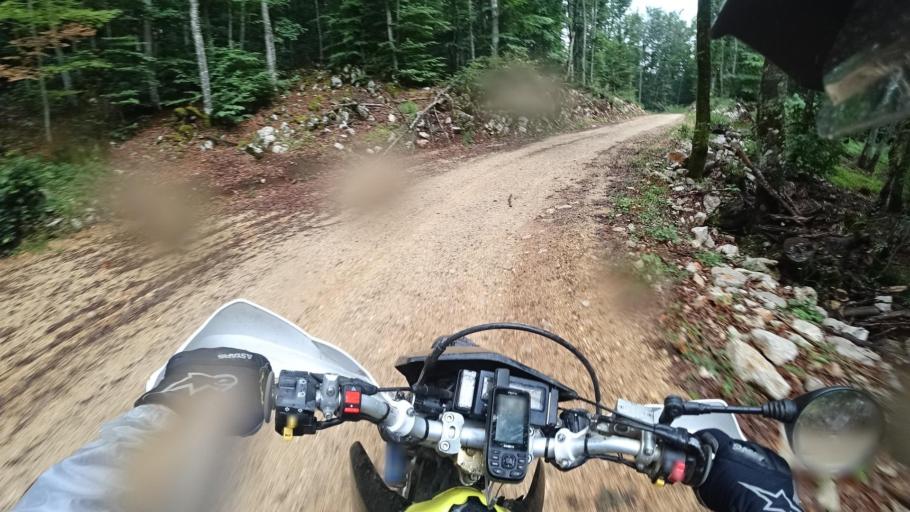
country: HR
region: Licko-Senjska
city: Jezerce
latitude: 44.7112
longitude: 15.6592
